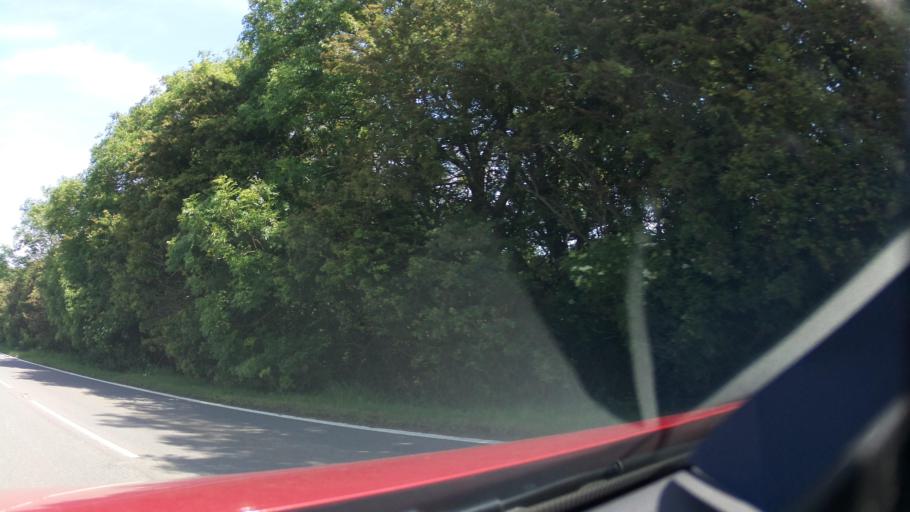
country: GB
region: England
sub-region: North Lincolnshire
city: Manton
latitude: 53.5044
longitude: -0.5821
